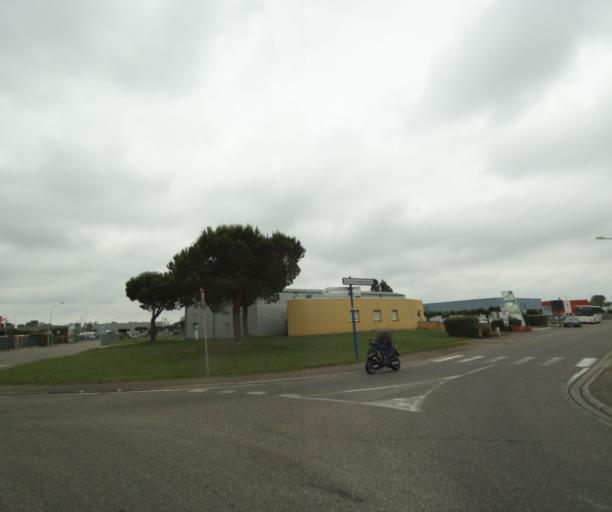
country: FR
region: Midi-Pyrenees
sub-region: Departement du Tarn-et-Garonne
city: Bressols
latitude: 43.9922
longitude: 1.3336
